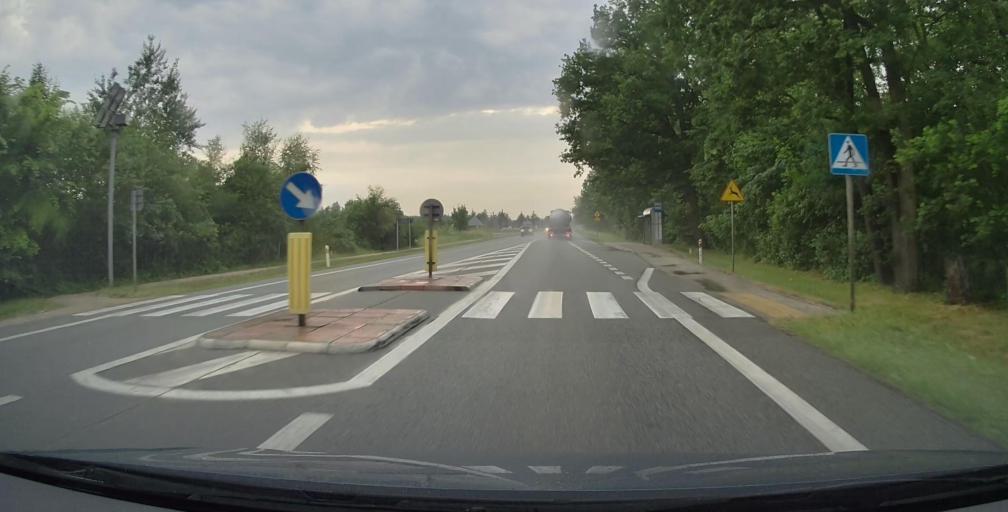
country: PL
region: Masovian Voivodeship
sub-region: Powiat siedlecki
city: Zbuczyn
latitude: 52.0839
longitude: 22.4625
